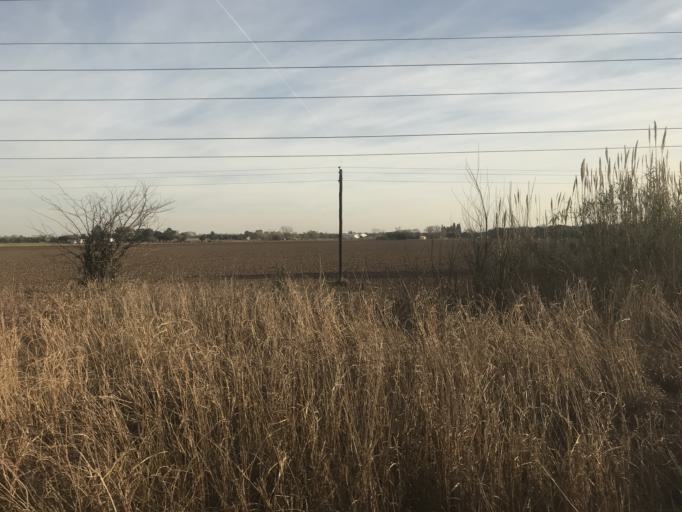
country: AR
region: Cordoba
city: Malvinas Argentinas
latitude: -31.4801
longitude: -64.0877
